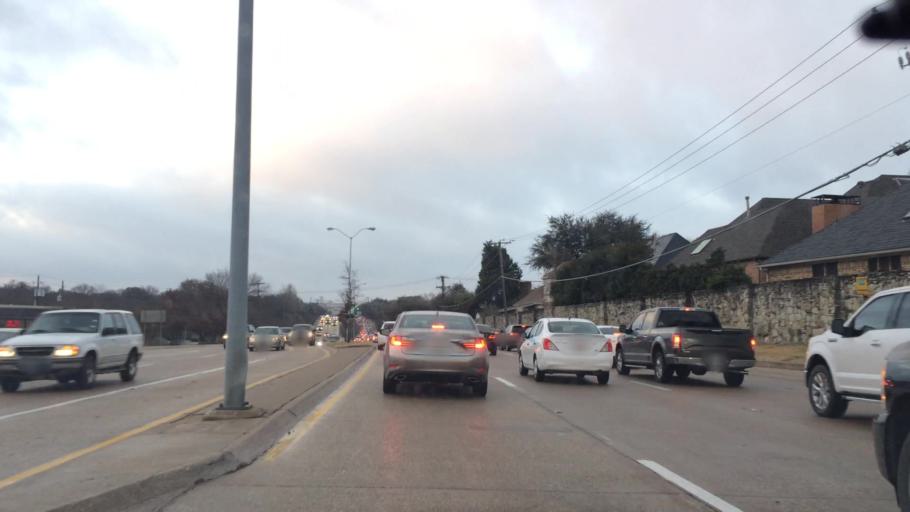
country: US
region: Texas
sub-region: Dallas County
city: Addison
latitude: 32.9674
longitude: -96.8045
